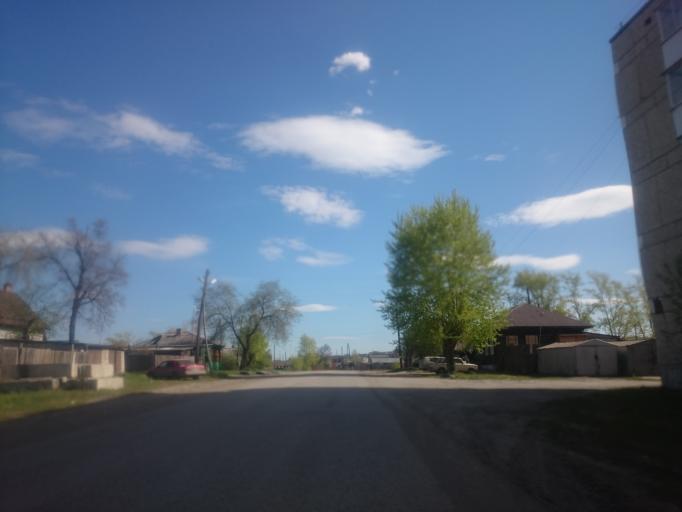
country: RU
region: Sverdlovsk
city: Irbit
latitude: 57.6700
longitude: 63.0649
